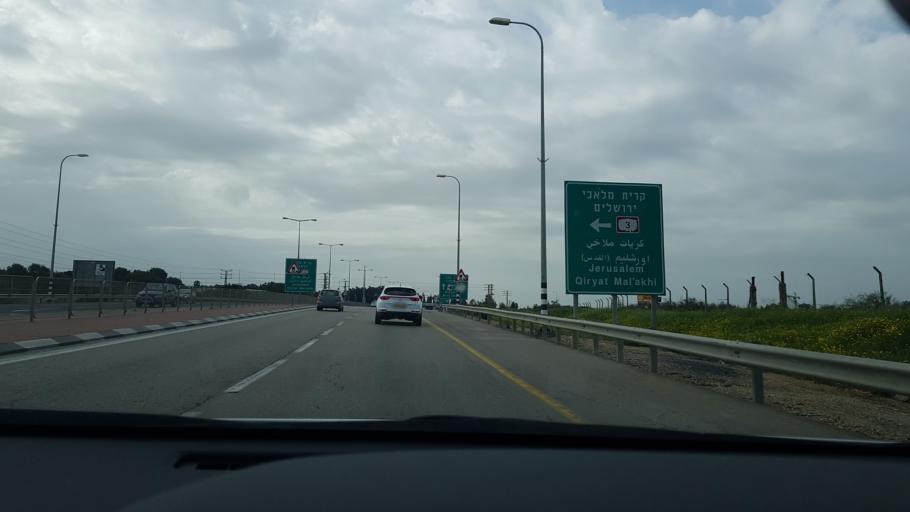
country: IL
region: Southern District
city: Ashqelon
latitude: 31.6789
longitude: 34.6097
